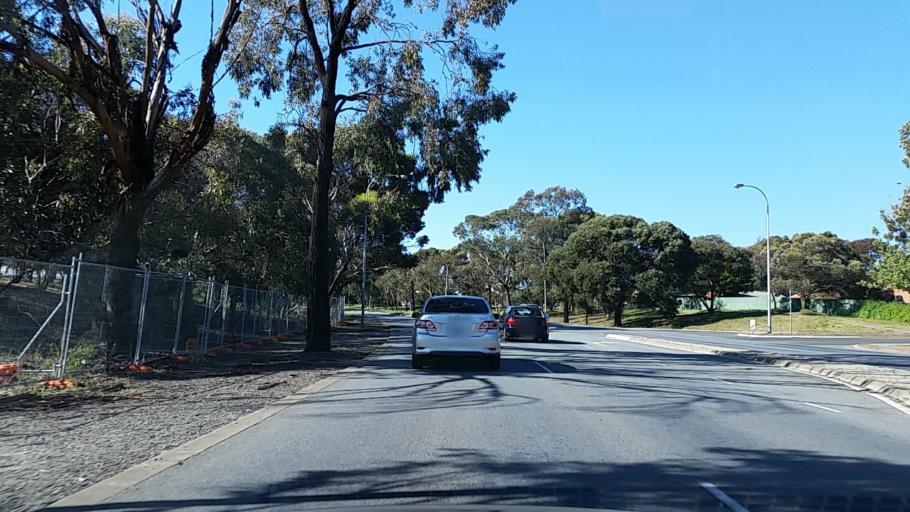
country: AU
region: South Australia
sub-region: Onkaparinga
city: Noarlunga Downs
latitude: -35.1431
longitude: 138.5022
